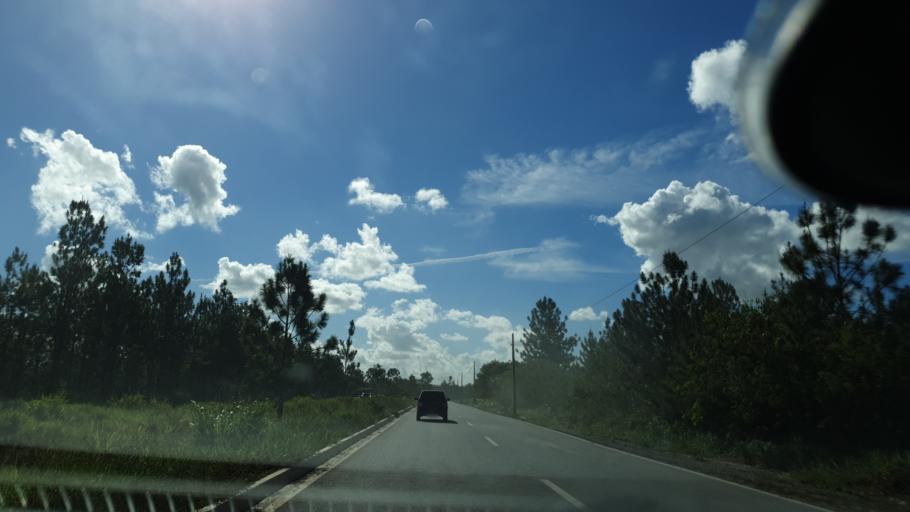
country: BR
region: Bahia
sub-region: Camacari
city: Camacari
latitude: -12.6825
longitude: -38.2988
